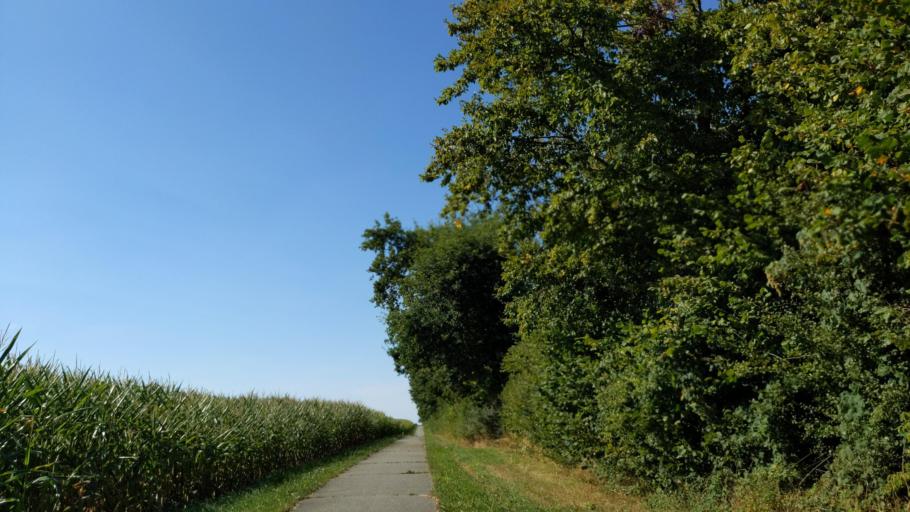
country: DE
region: Mecklenburg-Vorpommern
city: Selmsdorf
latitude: 53.8290
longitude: 10.8805
